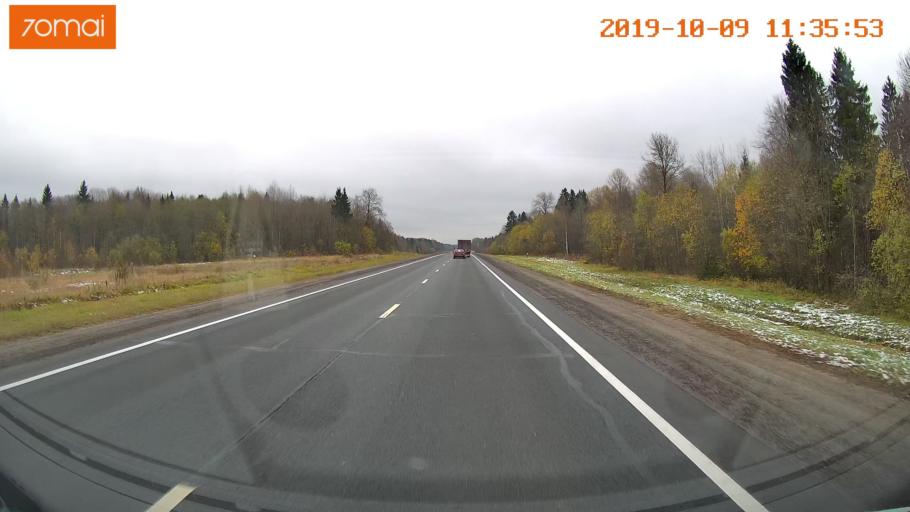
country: RU
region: Vologda
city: Gryazovets
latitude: 58.9978
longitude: 40.1307
